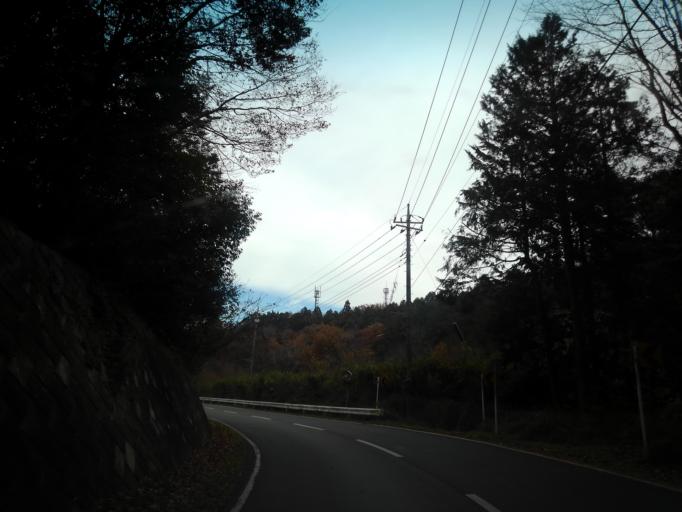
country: JP
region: Saitama
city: Morohongo
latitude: 35.9959
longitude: 139.2964
